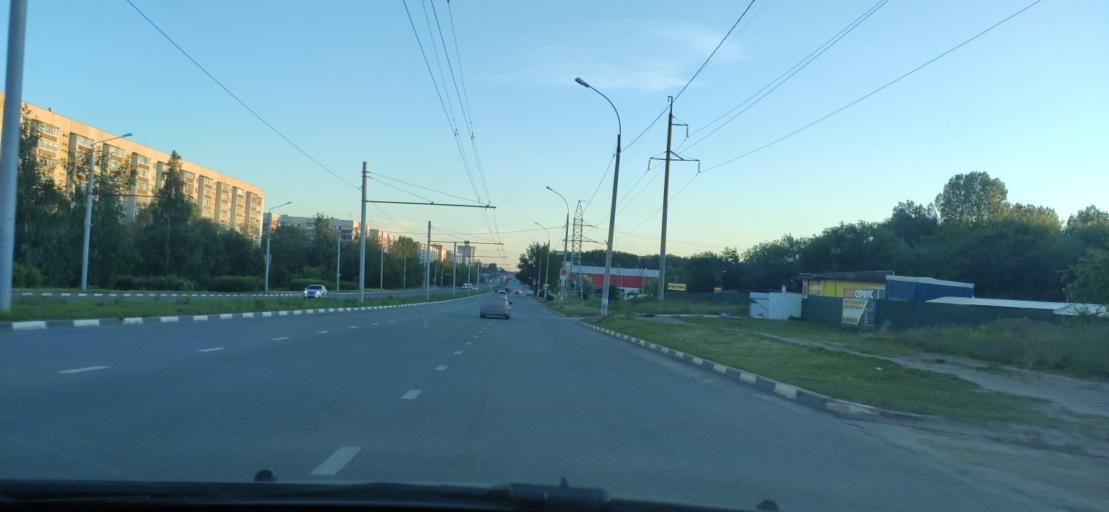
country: RU
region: Ulyanovsk
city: Mirnyy
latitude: 54.3862
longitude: 48.6059
